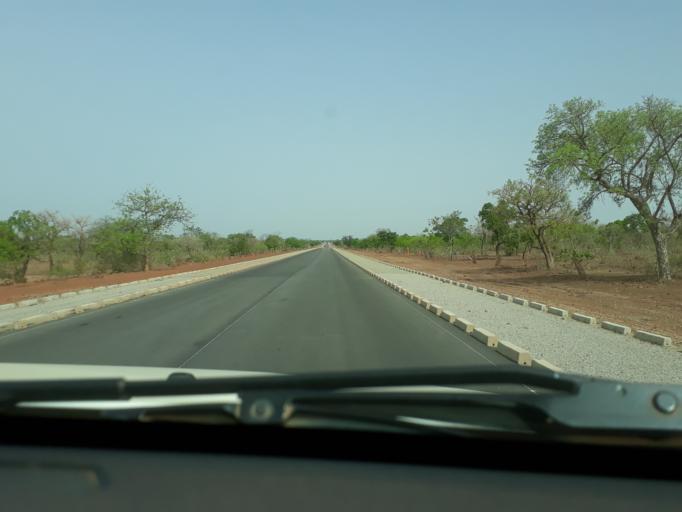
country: BF
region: Plateau-Central
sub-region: Province d'Oubritenga
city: Ziniare
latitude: 12.5504
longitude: -1.4073
